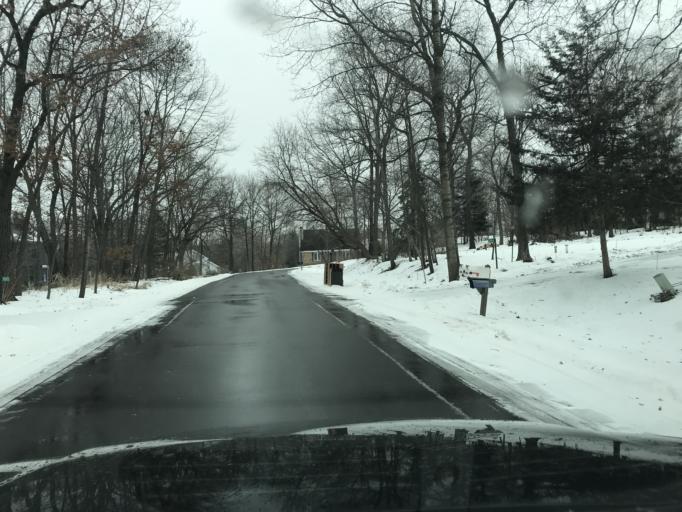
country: US
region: Wisconsin
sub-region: Dane County
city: Cottage Grove
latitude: 43.0874
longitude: -89.2230
